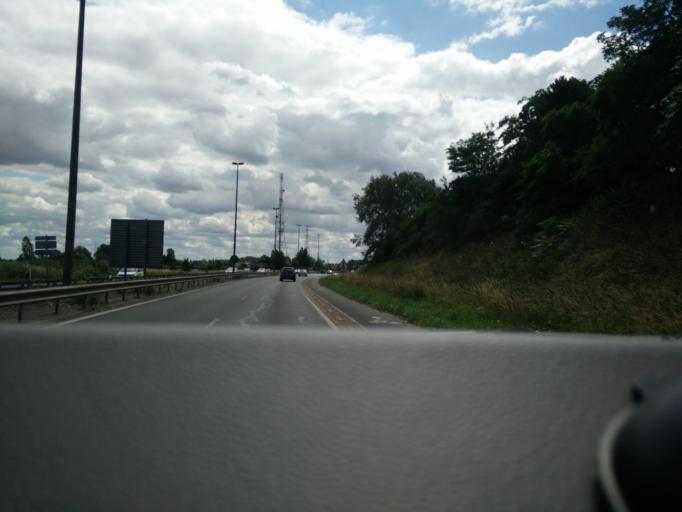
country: FR
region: Nord-Pas-de-Calais
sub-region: Departement du Nord
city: Coudekerque-Branche
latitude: 51.0337
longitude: 2.4064
